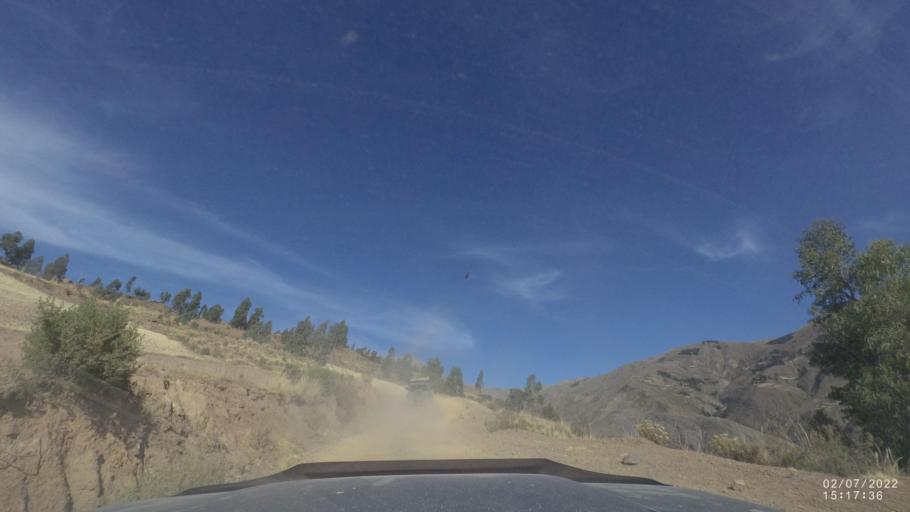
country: BO
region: Cochabamba
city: Irpa Irpa
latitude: -17.8671
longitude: -66.4323
